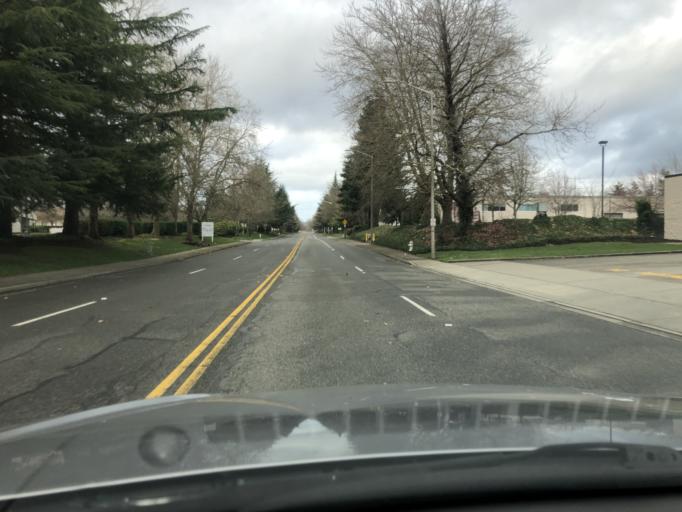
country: US
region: Washington
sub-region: King County
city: Kent
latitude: 47.4173
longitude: -122.2440
